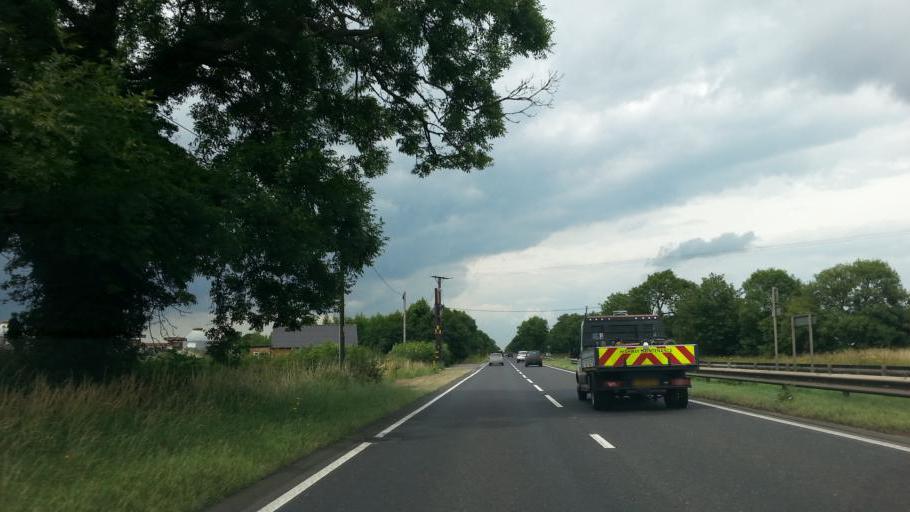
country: GB
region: England
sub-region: Leicestershire
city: Queniborough
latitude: 52.7607
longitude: -1.0565
